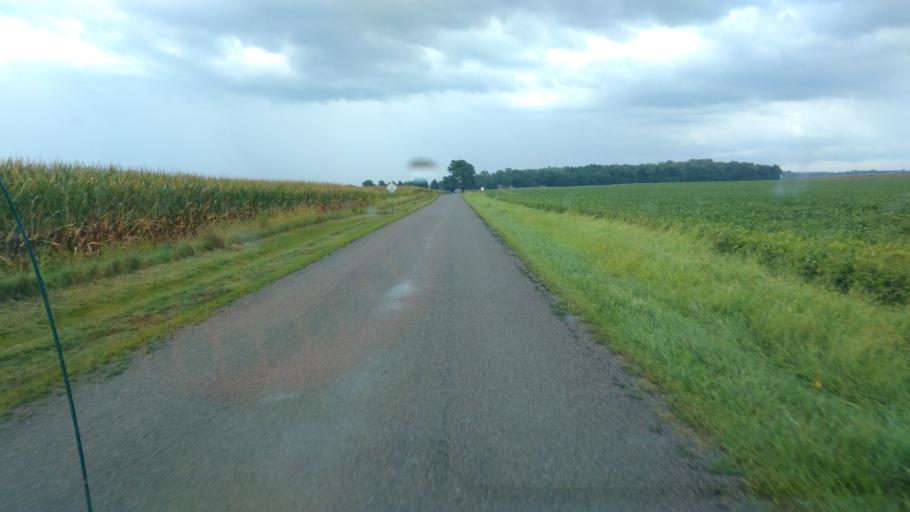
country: US
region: Ohio
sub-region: Hardin County
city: Kenton
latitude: 40.6891
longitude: -83.6148
